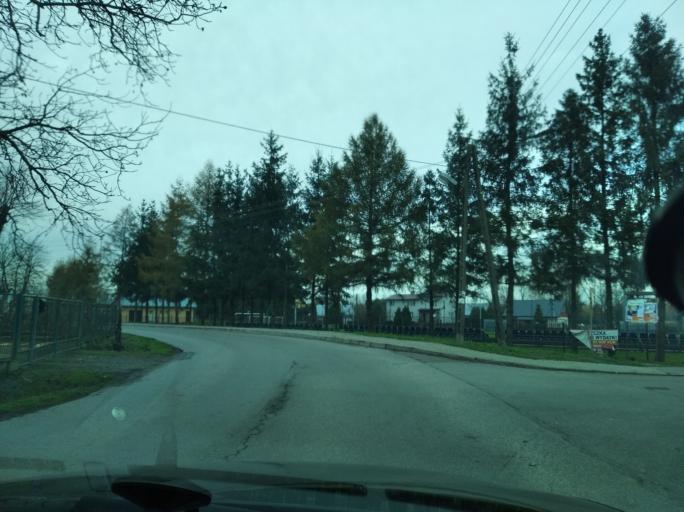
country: PL
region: Subcarpathian Voivodeship
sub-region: Powiat przeworski
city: Grzeska
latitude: 50.0830
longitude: 22.4533
